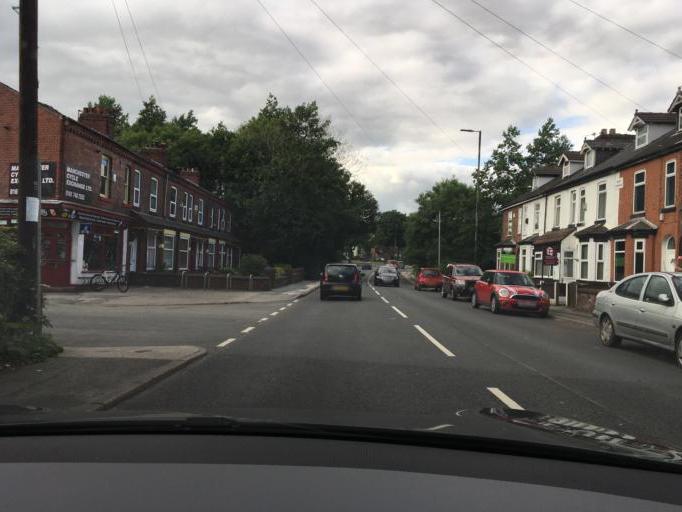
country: GB
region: England
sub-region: Trafford
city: Urmston
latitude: 53.4587
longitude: -2.3578
